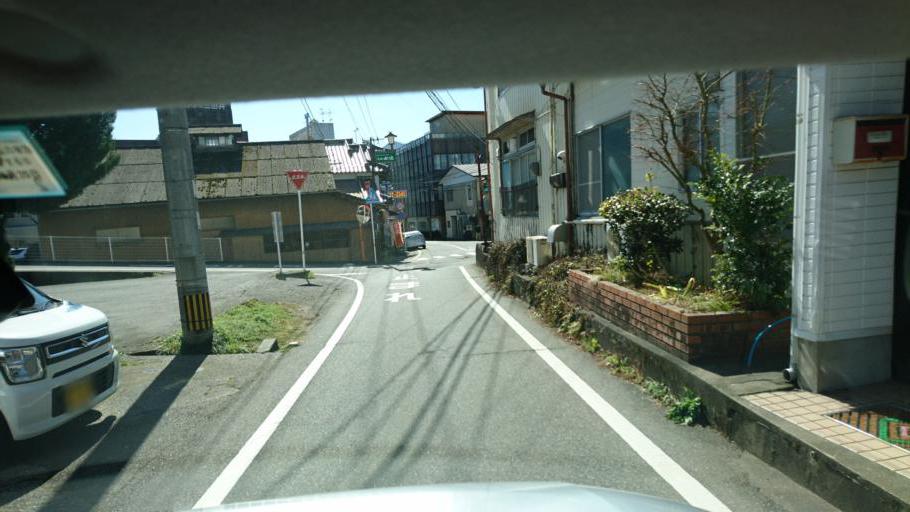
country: JP
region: Oita
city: Takedamachi
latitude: 32.7114
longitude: 131.3088
